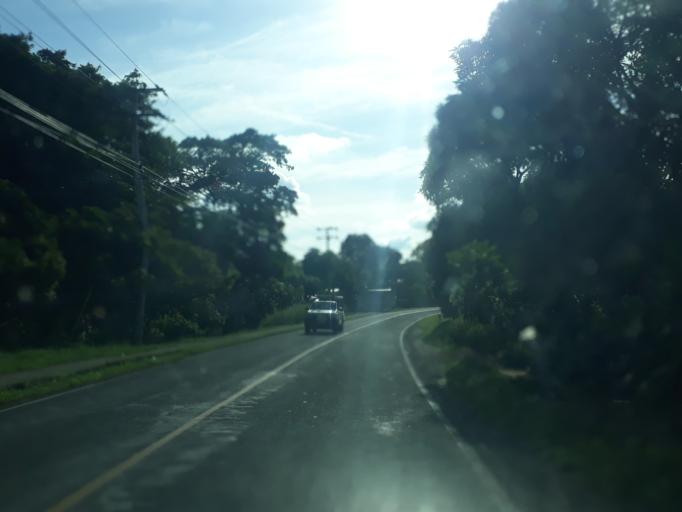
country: NI
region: Masaya
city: Masatepe
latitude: 11.9045
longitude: -86.1612
